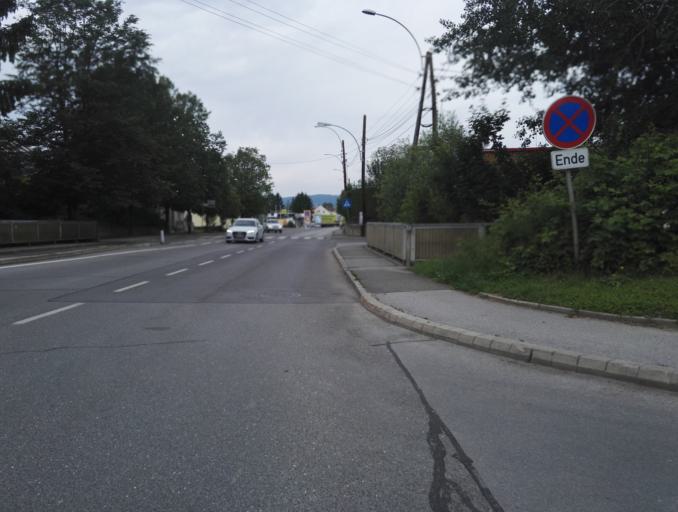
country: AT
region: Styria
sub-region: Graz Stadt
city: Mariatrost
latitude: 47.0772
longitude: 15.4942
